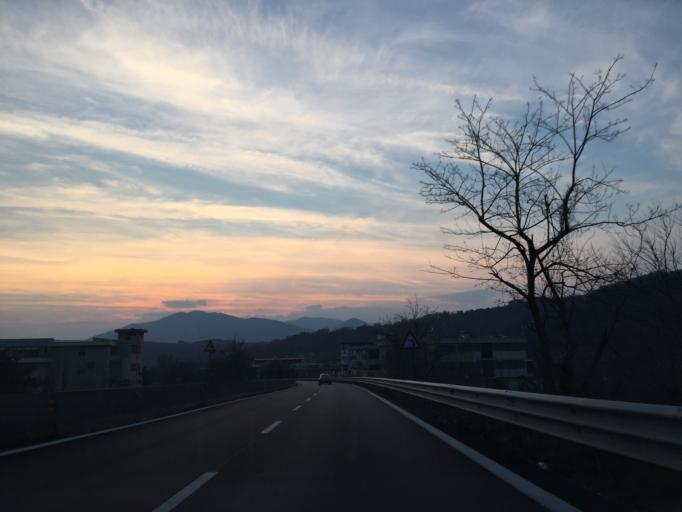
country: IT
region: Campania
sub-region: Provincia di Avellino
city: Solofra
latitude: 40.8339
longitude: 14.8296
